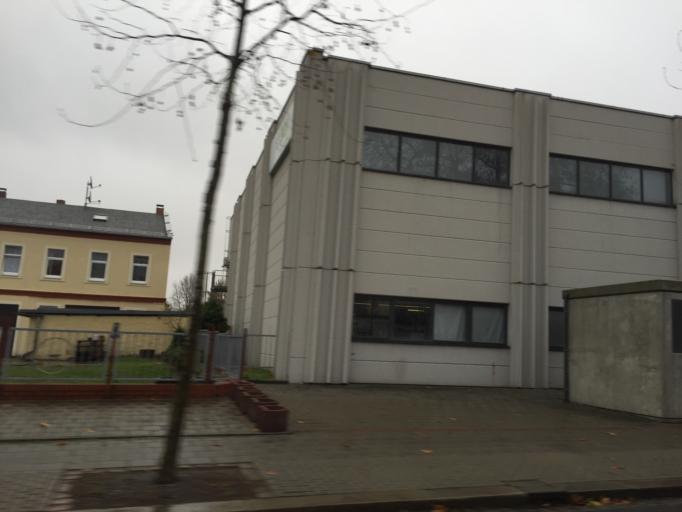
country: DE
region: Saxony
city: Dresden
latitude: 51.0391
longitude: 13.7050
